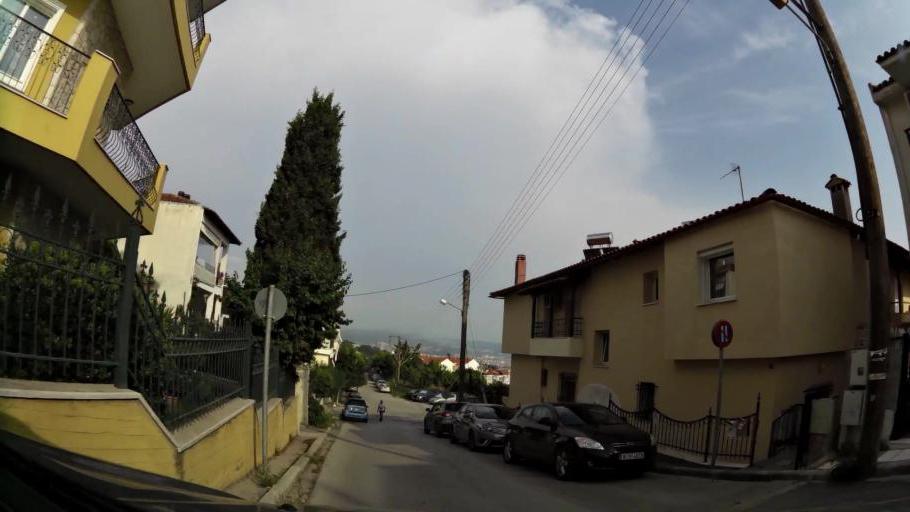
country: GR
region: Central Macedonia
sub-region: Nomos Thessalonikis
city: Oraiokastro
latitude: 40.7215
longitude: 22.9156
